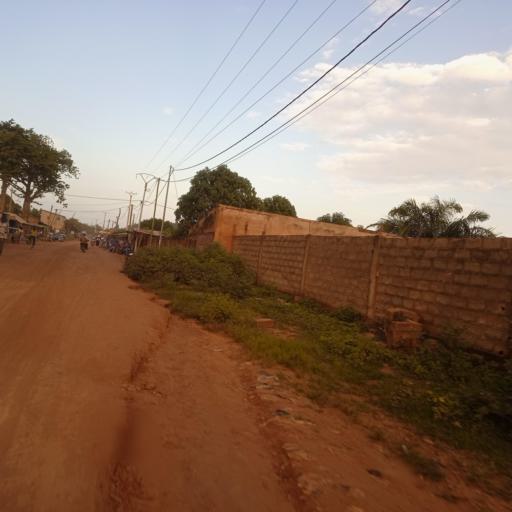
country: TG
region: Savanes
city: Dapaong
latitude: 10.8617
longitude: 0.1845
